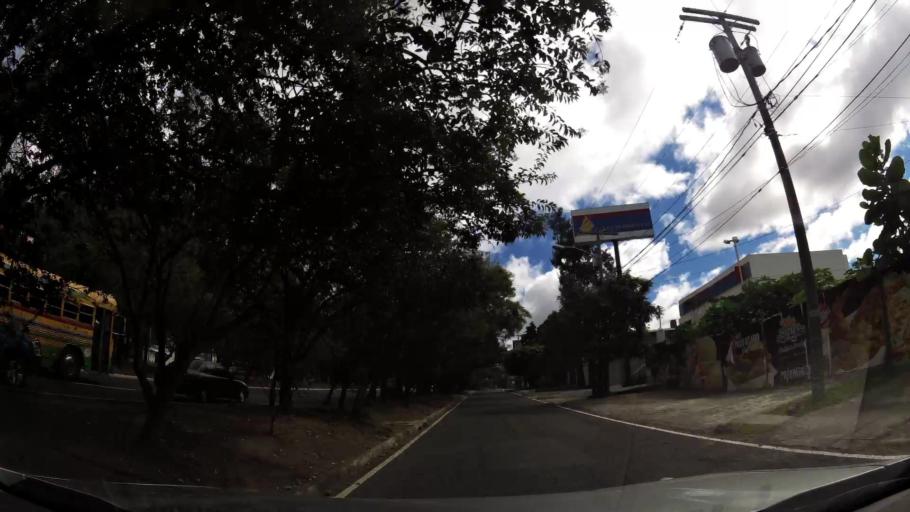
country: GT
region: Guatemala
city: Santa Catarina Pinula
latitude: 14.5905
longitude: -90.4919
